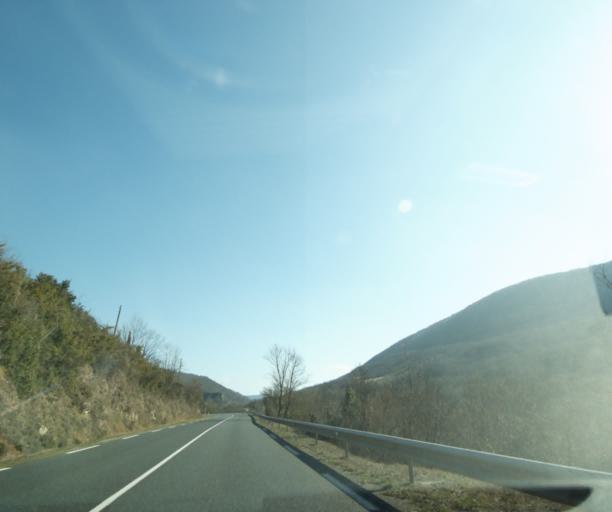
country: FR
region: Midi-Pyrenees
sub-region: Departement de l'Aveyron
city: Saint-Affrique
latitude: 43.9525
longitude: 2.9206
